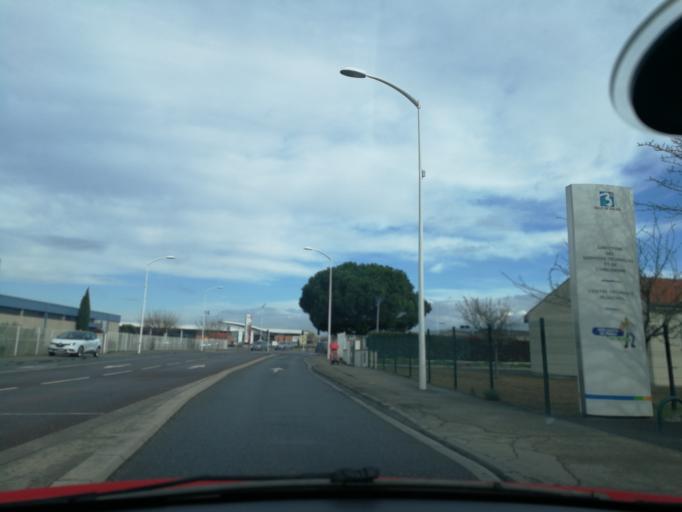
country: FR
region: Midi-Pyrenees
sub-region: Departement de la Haute-Garonne
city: Balma
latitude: 43.6129
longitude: 1.4889
